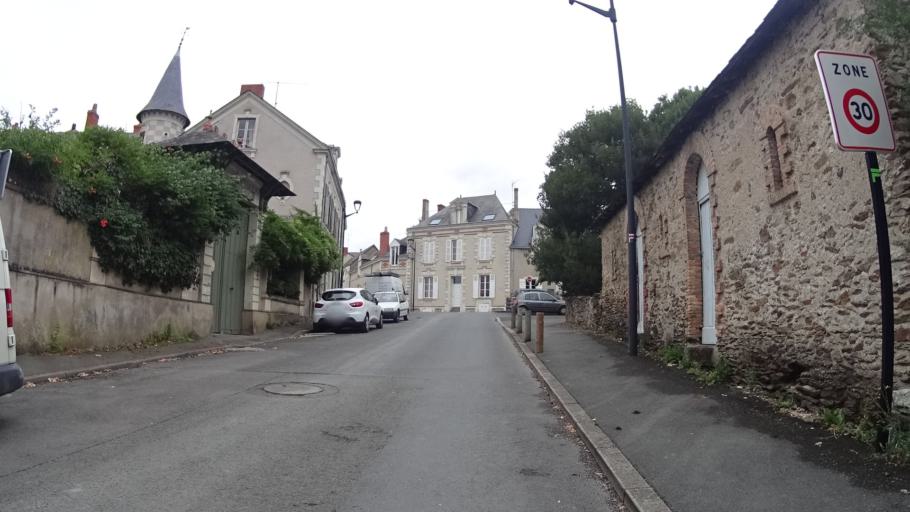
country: FR
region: Pays de la Loire
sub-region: Departement de Maine-et-Loire
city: La Possonniere
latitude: 47.3735
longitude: -0.6850
